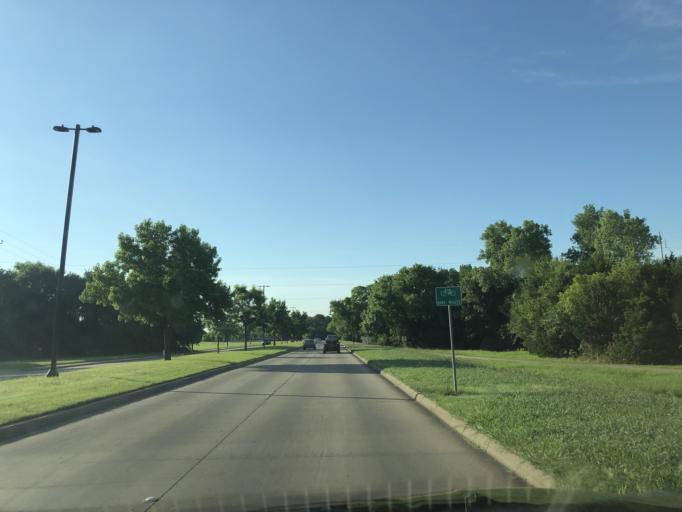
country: US
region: Texas
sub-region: Dallas County
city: Garland
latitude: 32.8507
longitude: -96.6098
